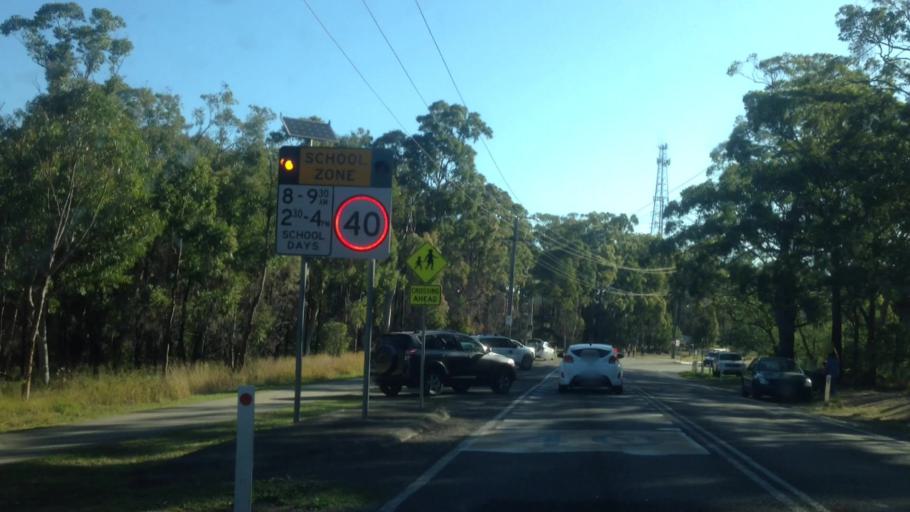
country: AU
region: New South Wales
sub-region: Lake Macquarie Shire
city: Dora Creek
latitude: -33.1128
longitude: 151.5186
